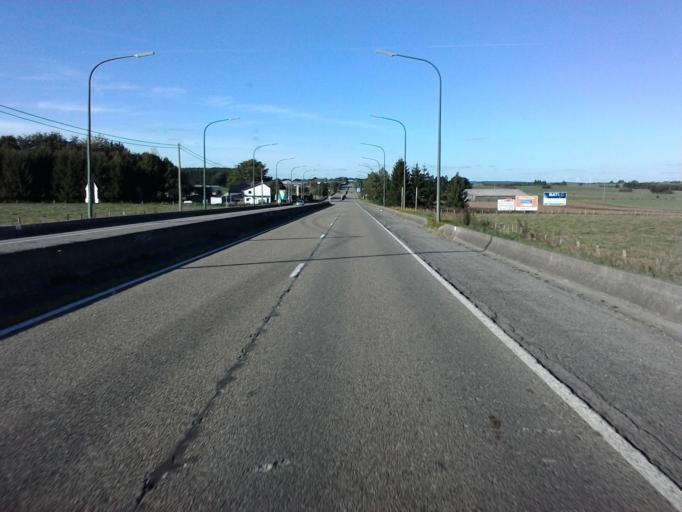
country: BE
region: Wallonia
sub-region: Province du Luxembourg
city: Bastogne
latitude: 49.9691
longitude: 5.7168
